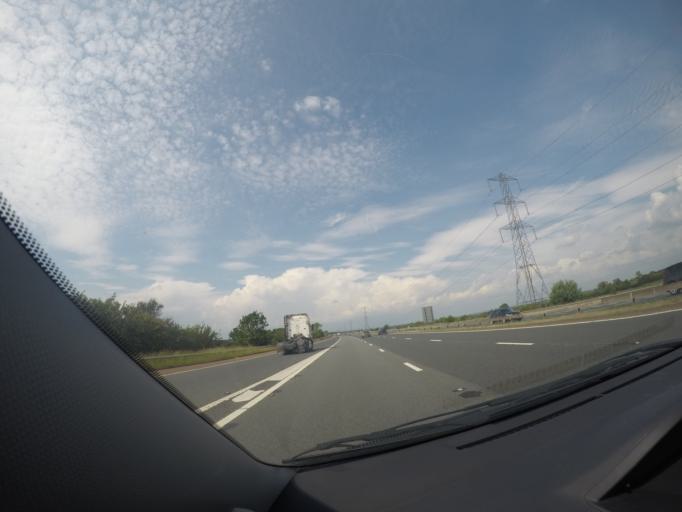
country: GB
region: England
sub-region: Cumbria
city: Scotby
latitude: 54.8983
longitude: -2.8873
